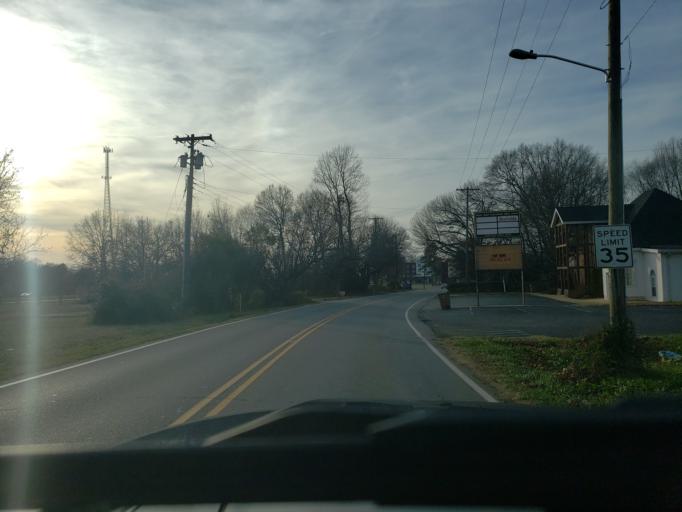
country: US
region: North Carolina
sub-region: Cleveland County
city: Shelby
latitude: 35.2743
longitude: -81.4994
